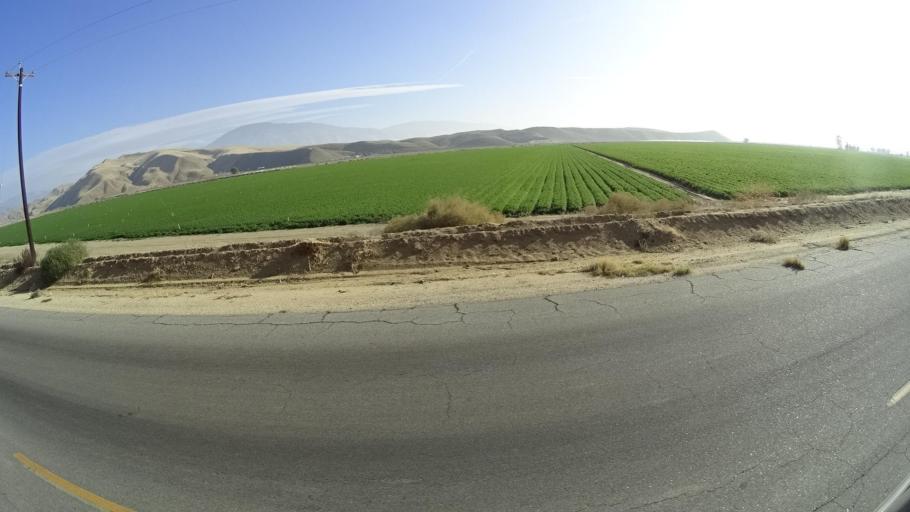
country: US
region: California
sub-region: Kern County
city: Arvin
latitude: 35.3285
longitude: -118.7660
